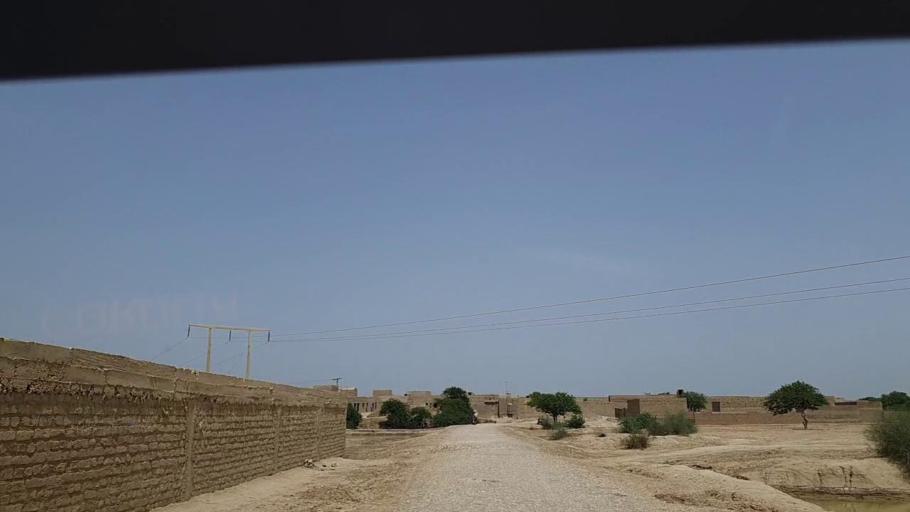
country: PK
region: Sindh
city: Johi
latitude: 26.7156
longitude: 67.6500
